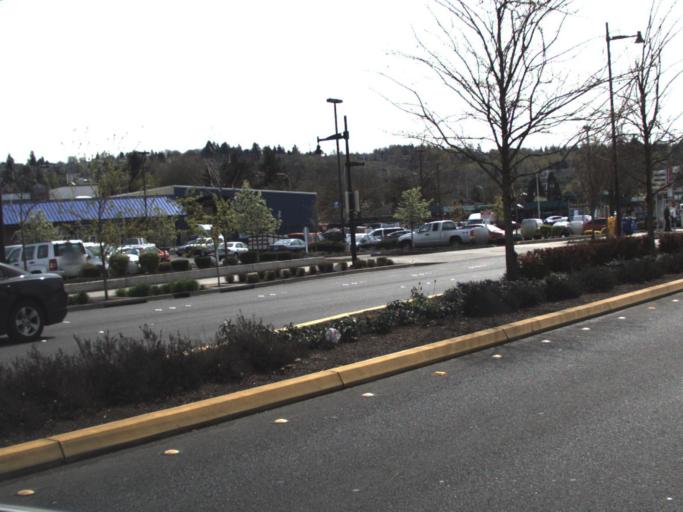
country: US
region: Washington
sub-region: King County
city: Renton
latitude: 47.4775
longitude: -122.2159
